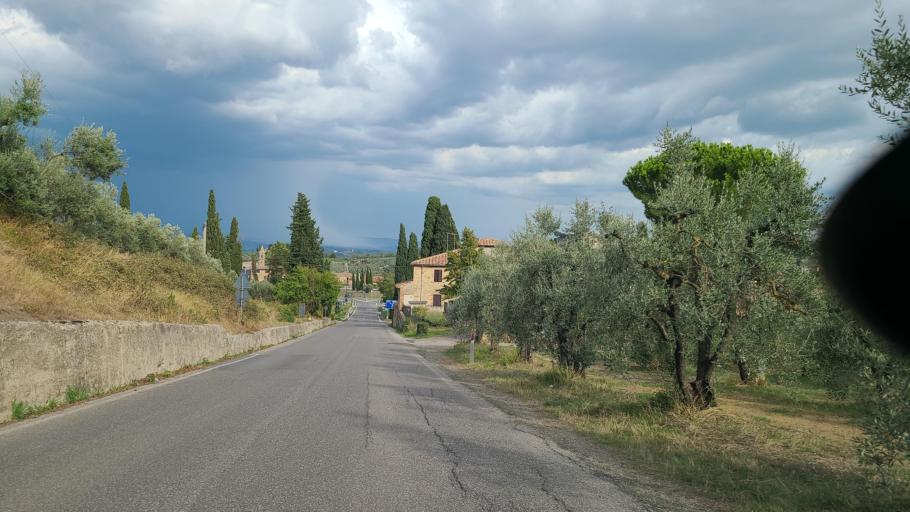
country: IT
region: Tuscany
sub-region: Provincia di Siena
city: San Gimignano
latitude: 43.4770
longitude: 11.0259
